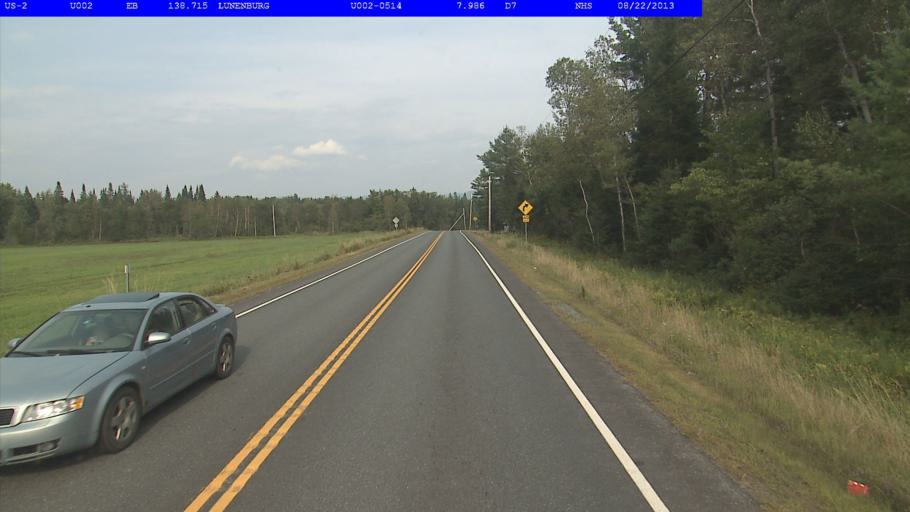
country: US
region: New Hampshire
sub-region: Coos County
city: Lancaster
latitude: 44.4850
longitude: -71.6308
